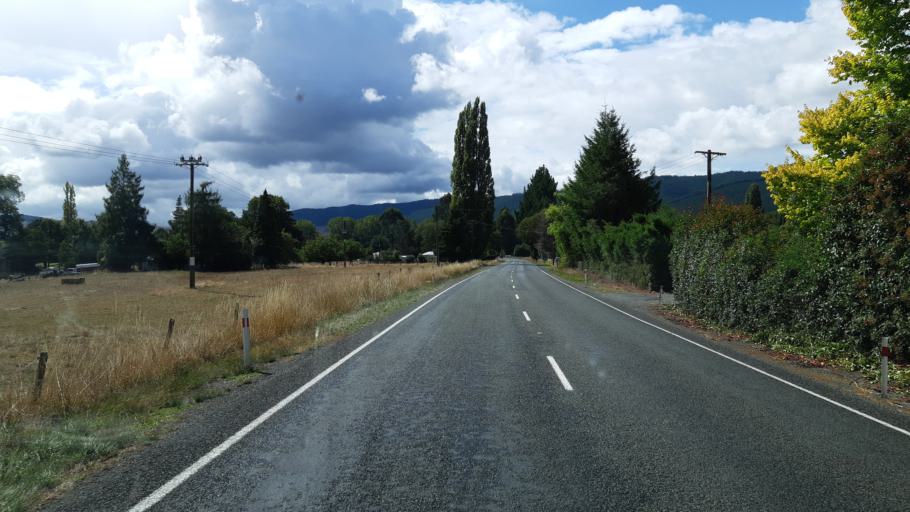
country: NZ
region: Tasman
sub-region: Tasman District
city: Wakefield
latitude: -41.4547
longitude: 172.8152
